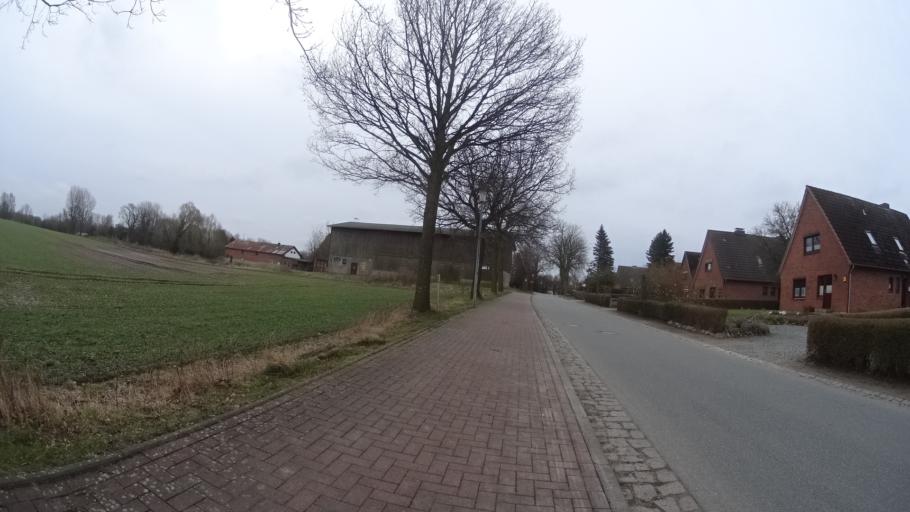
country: DE
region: Schleswig-Holstein
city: Stakendorf
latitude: 54.3915
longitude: 10.4208
